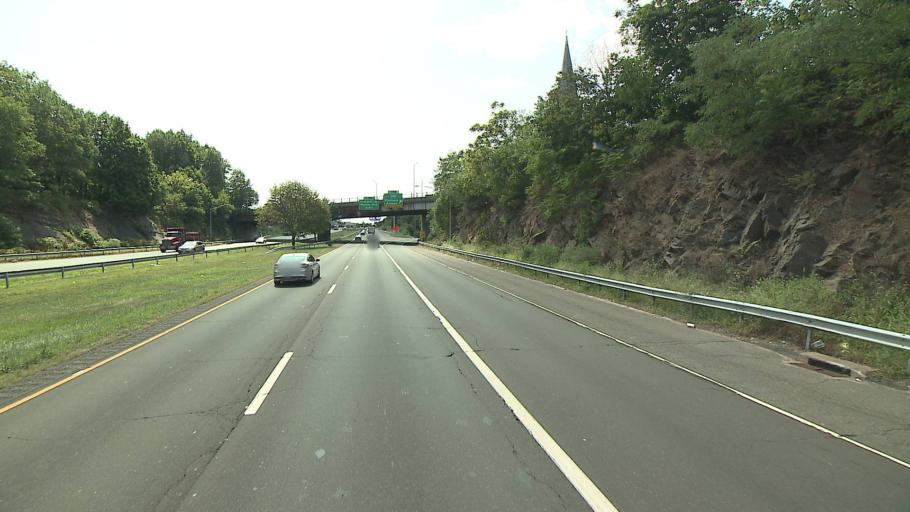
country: US
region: Connecticut
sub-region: Fairfield County
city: Bridgeport
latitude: 41.1812
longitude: -73.1944
